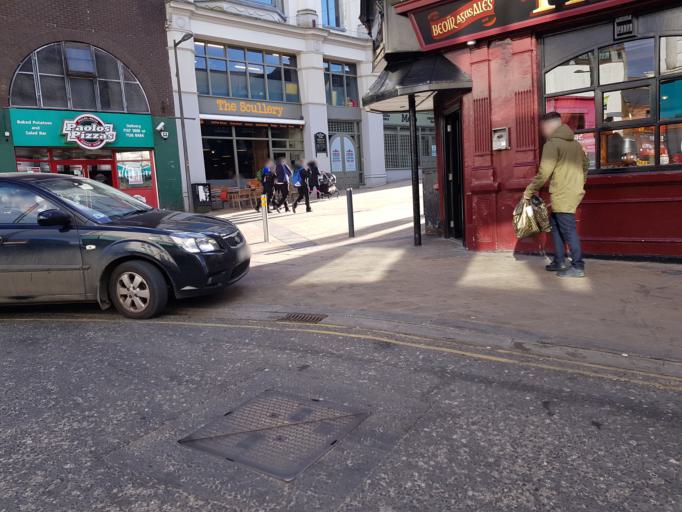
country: GB
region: Northern Ireland
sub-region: City of Derry
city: Derry
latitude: 54.9976
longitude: -7.3218
